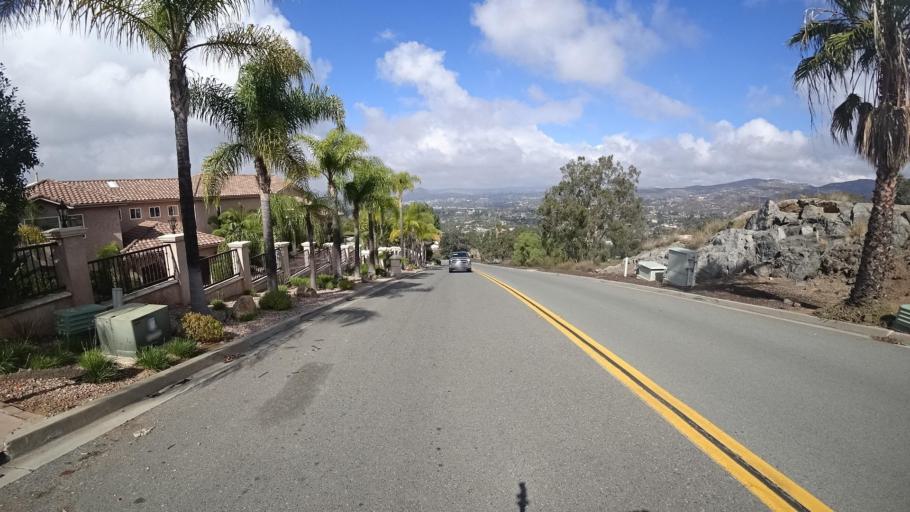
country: US
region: California
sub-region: San Diego County
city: Granite Hills
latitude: 32.7751
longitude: -116.8987
